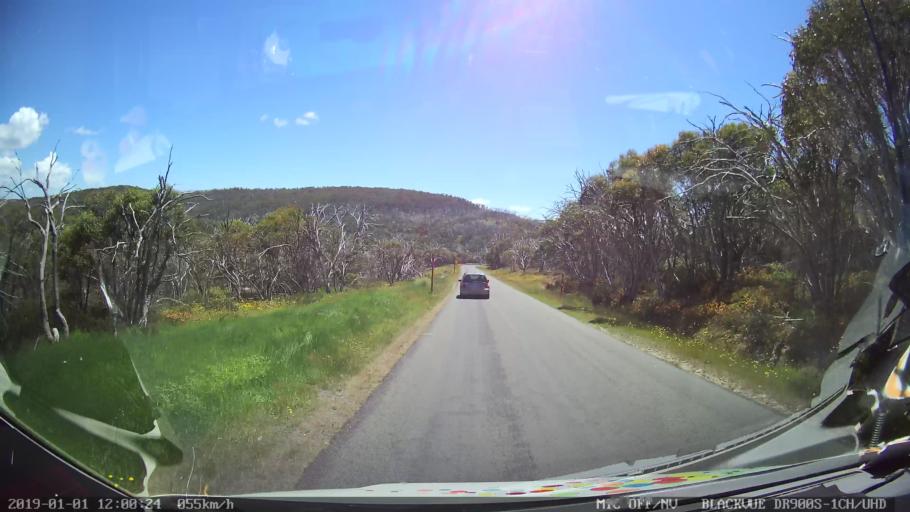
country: AU
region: New South Wales
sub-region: Snowy River
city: Jindabyne
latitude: -35.8851
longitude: 148.4592
